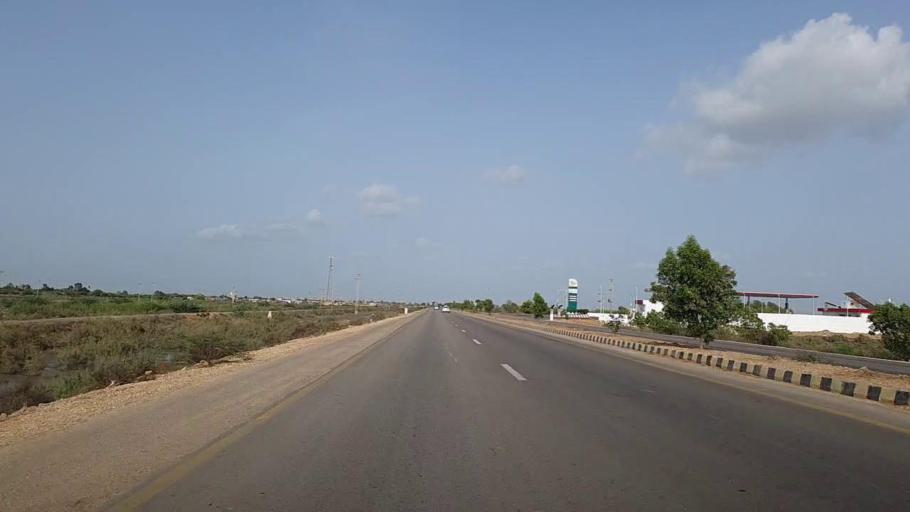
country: PK
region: Sindh
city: Gharo
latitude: 24.7397
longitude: 67.7461
